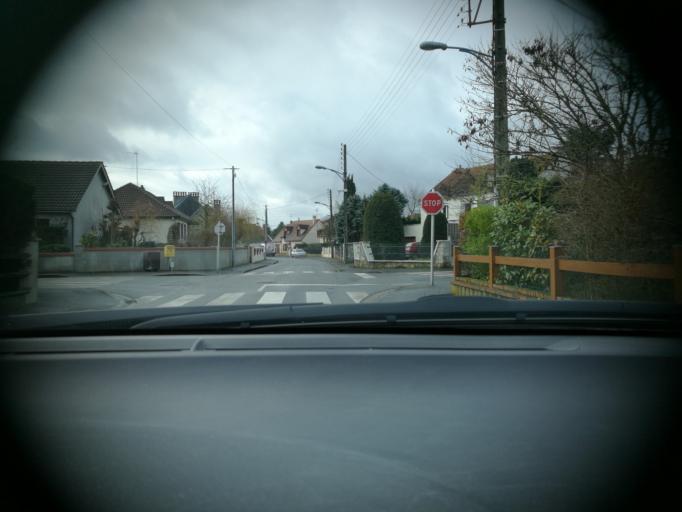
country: FR
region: Centre
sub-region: Departement du Loiret
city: Fleury-les-Aubrais
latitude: 47.9390
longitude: 1.9057
